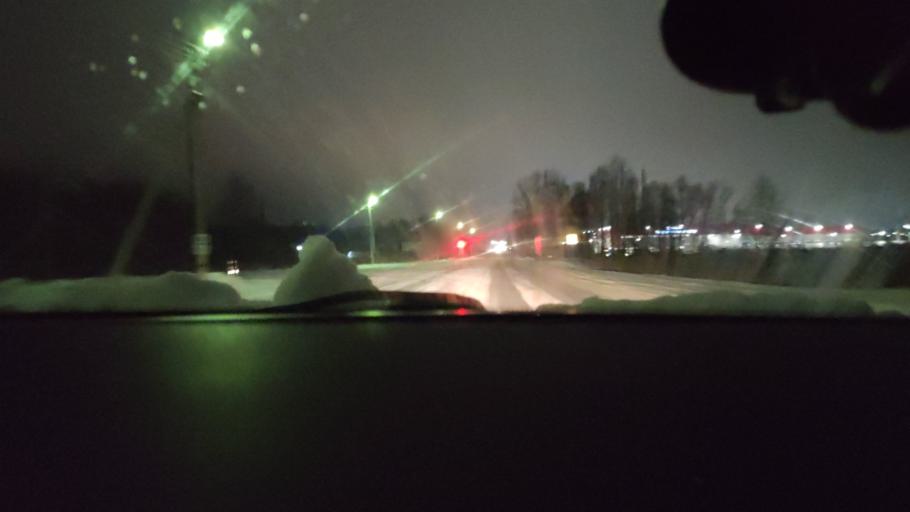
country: RU
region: Perm
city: Overyata
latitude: 58.0580
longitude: 55.8439
